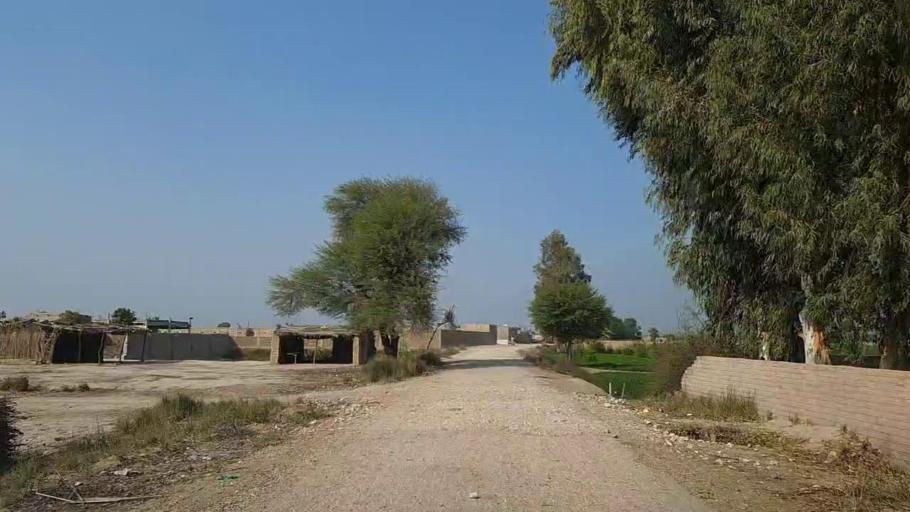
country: PK
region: Sindh
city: Moro
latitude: 26.6882
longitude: 67.9482
